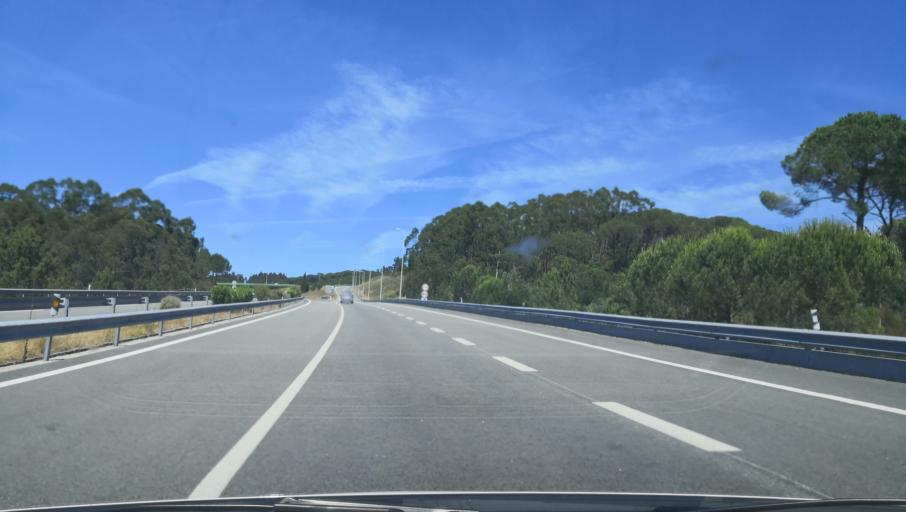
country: PT
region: Coimbra
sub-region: Montemor-O-Velho
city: Montemor-o-Velho
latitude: 40.1990
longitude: -8.6787
